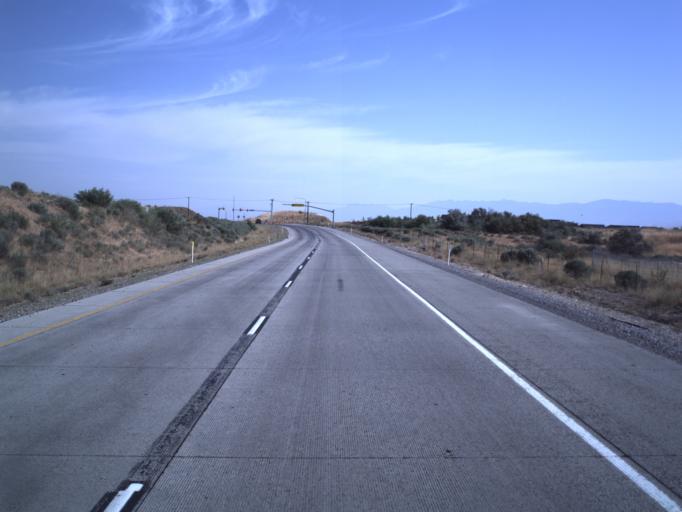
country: US
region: Utah
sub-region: Salt Lake County
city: Oquirrh
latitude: 40.6346
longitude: -112.0451
